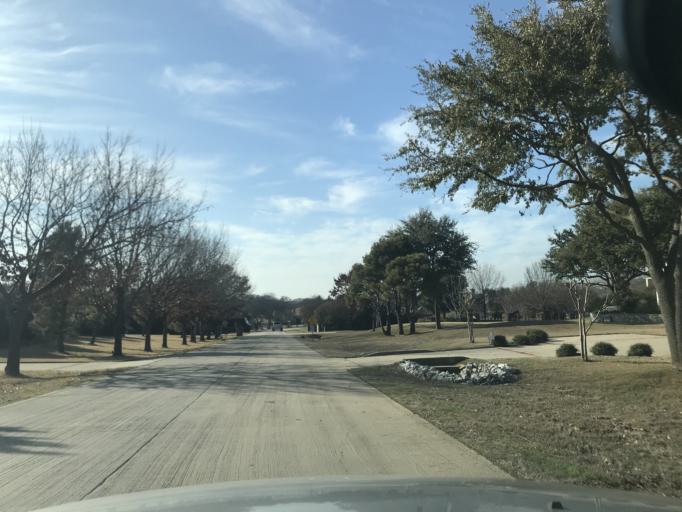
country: US
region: Texas
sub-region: Collin County
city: Frisco
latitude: 33.0948
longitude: -96.8281
